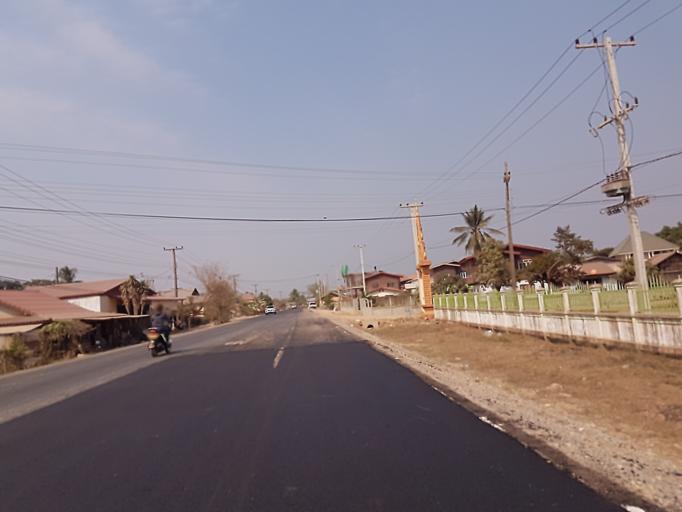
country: TH
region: Nong Khai
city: Nong Khai
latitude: 17.9241
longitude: 102.7693
